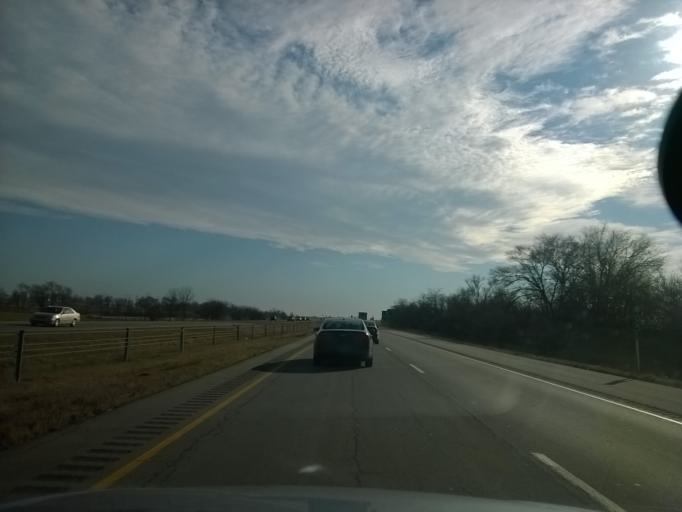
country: US
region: Indiana
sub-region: Johnson County
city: Edinburgh
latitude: 39.3711
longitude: -85.9427
